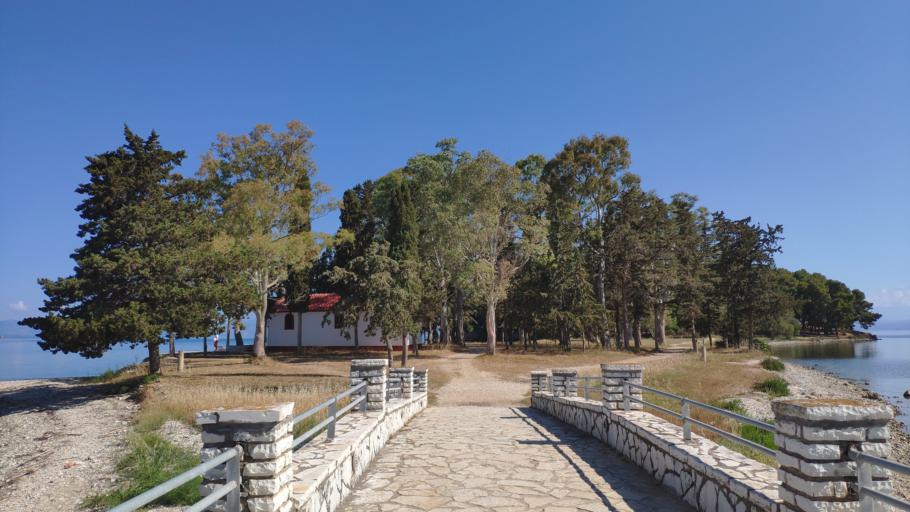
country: GR
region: West Greece
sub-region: Nomos Aitolias kai Akarnanias
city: Vonitsa
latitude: 38.9241
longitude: 20.9001
